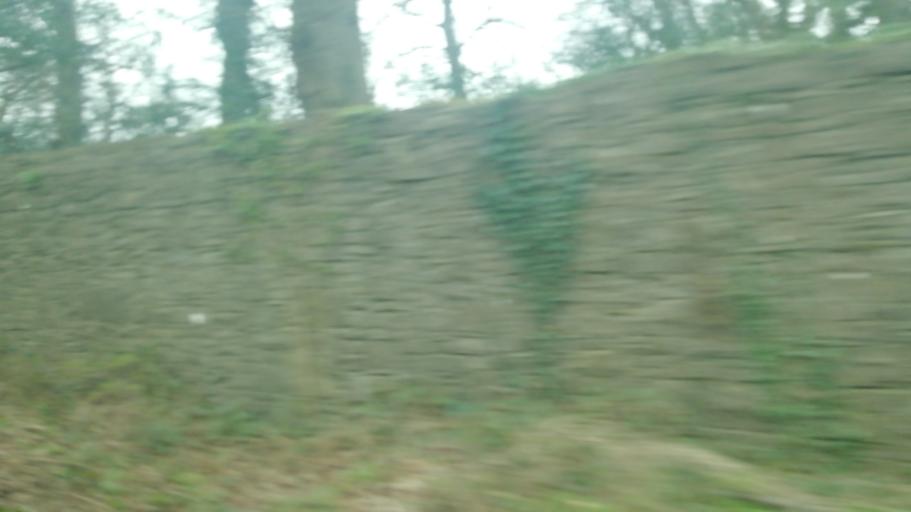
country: IE
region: Leinster
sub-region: Kildare
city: Celbridge
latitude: 53.3295
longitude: -6.5736
